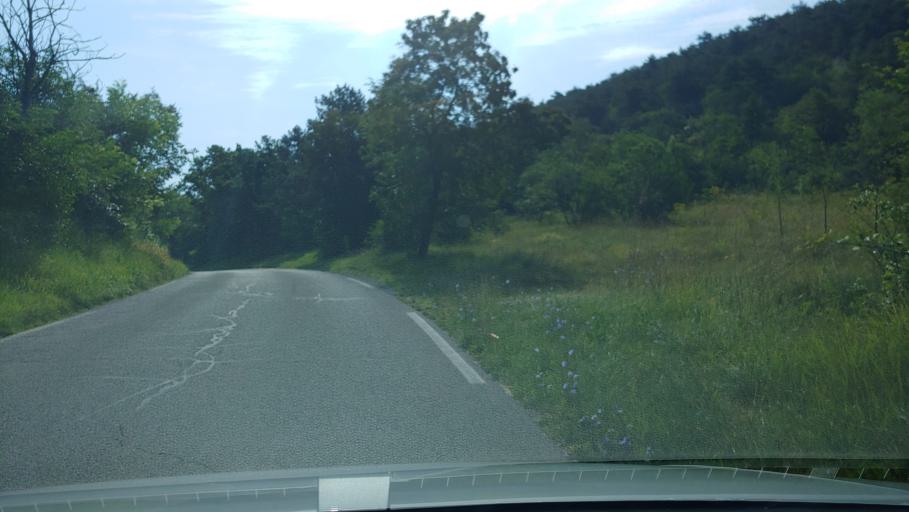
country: SI
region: Komen
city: Komen
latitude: 45.8442
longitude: 13.7756
